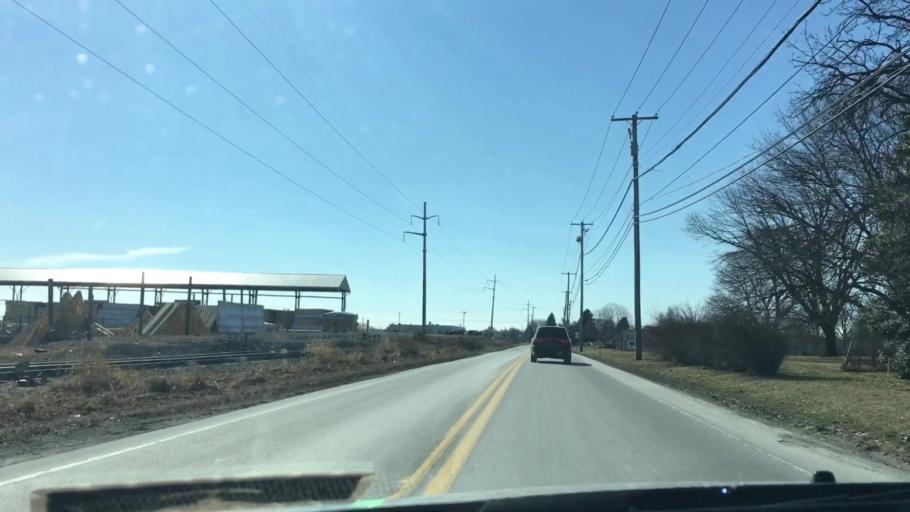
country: US
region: Pennsylvania
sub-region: Lancaster County
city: Brownstown
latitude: 40.0848
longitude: -76.1842
